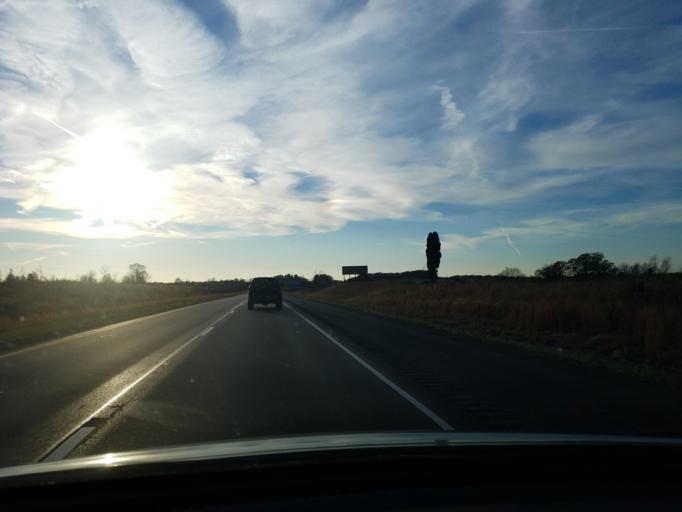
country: US
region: Indiana
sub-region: Spencer County
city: Dale
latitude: 38.1987
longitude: -86.9328
